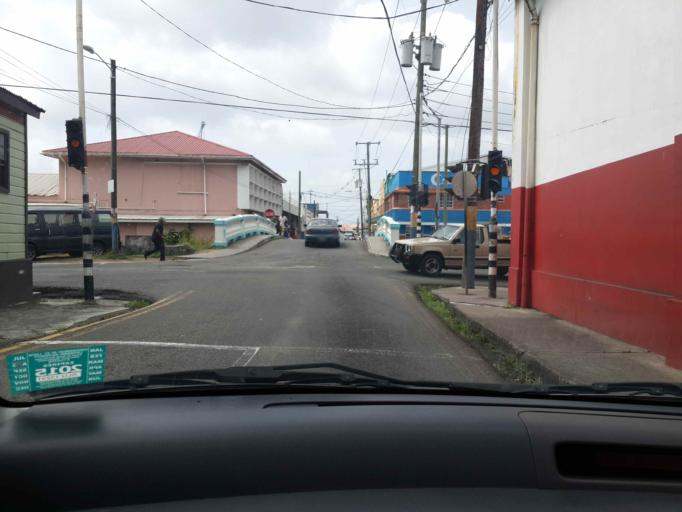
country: LC
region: Castries Quarter
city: Castries
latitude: 14.0081
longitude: -60.9925
